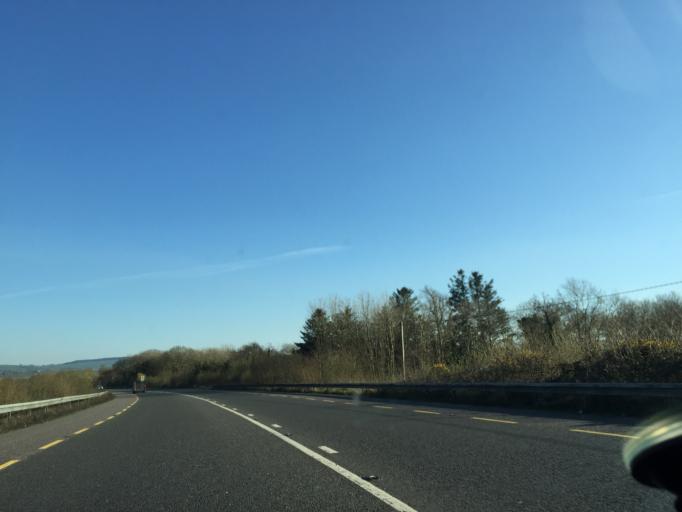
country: IE
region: Munster
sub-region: Ciarrai
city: Castleisland
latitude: 52.1970
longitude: -9.5706
